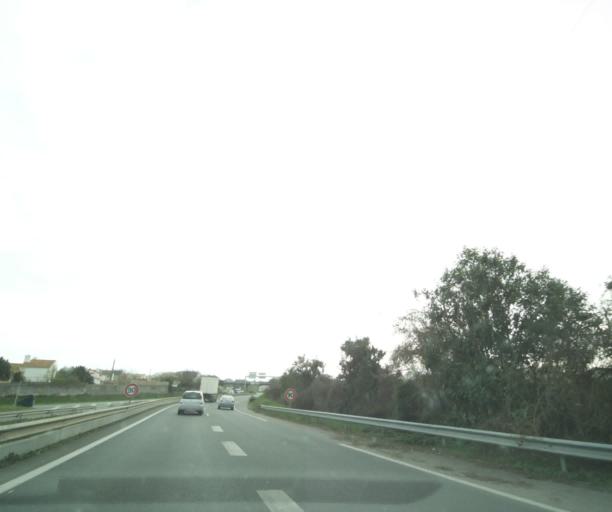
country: FR
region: Poitou-Charentes
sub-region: Departement de la Charente-Maritime
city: La Rochelle
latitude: 46.1694
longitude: -1.1908
